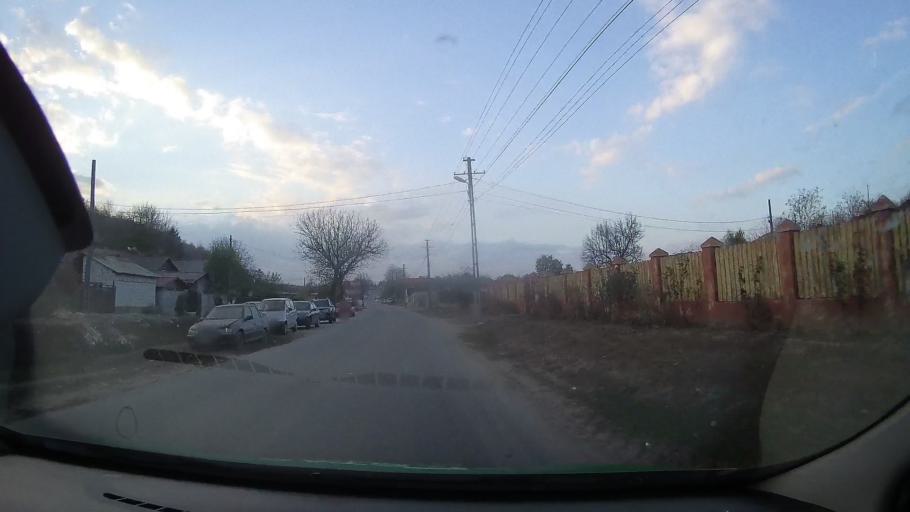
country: RO
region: Constanta
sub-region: Comuna Baneasa
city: Baneasa
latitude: 44.0616
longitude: 27.7059
